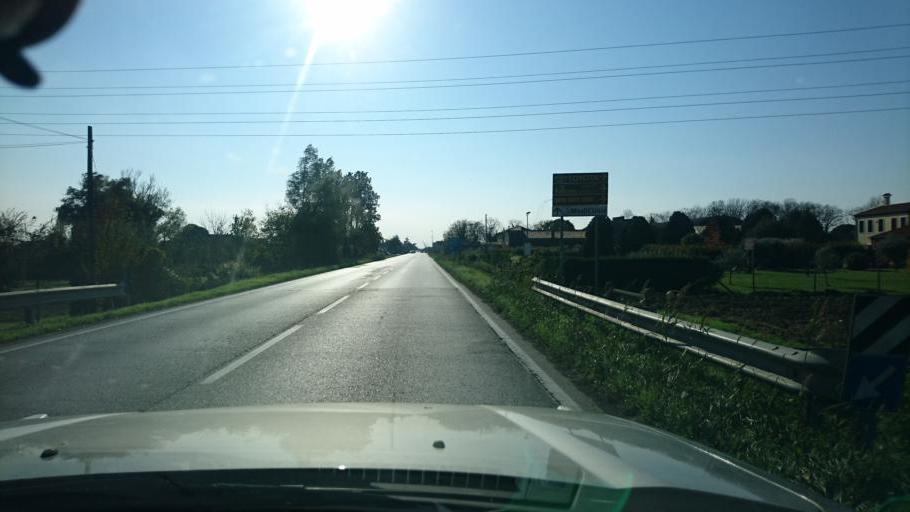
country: IT
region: Veneto
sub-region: Provincia di Padova
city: Monselice
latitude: 45.2234
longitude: 11.7551
